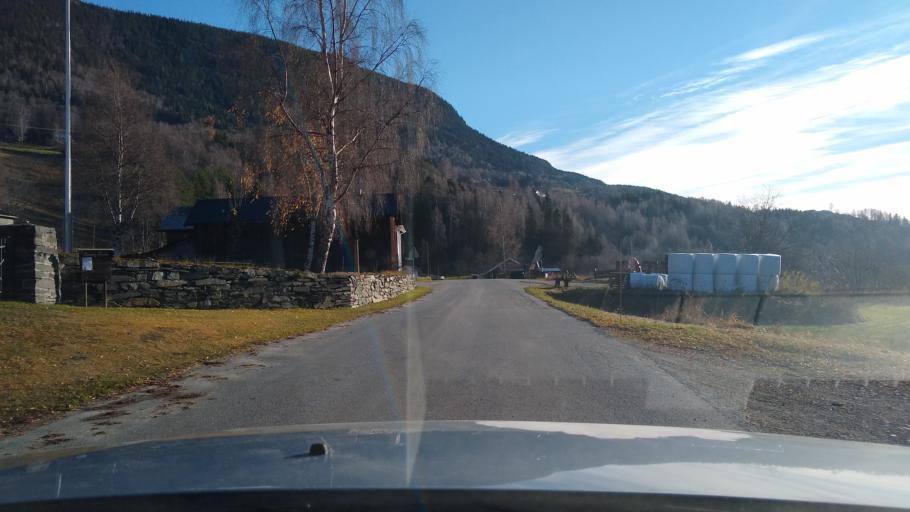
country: NO
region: Oppland
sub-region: Ringebu
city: Ringebu
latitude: 61.4270
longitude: 10.2197
